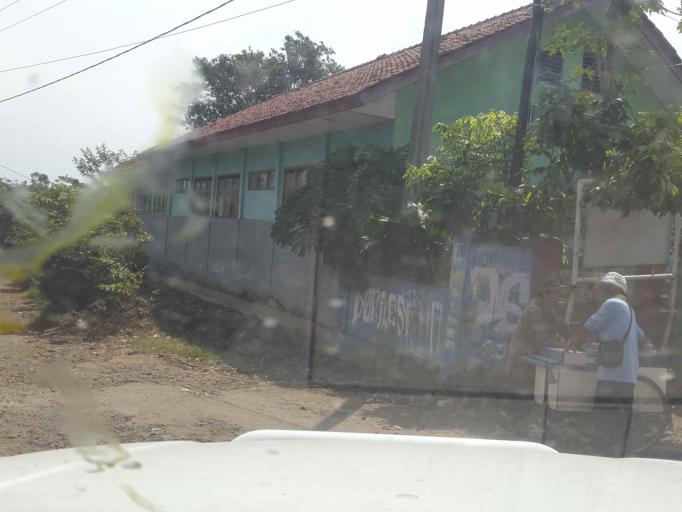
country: ID
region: West Java
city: Ciranjang-hilir
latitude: -6.8814
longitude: 107.2176
